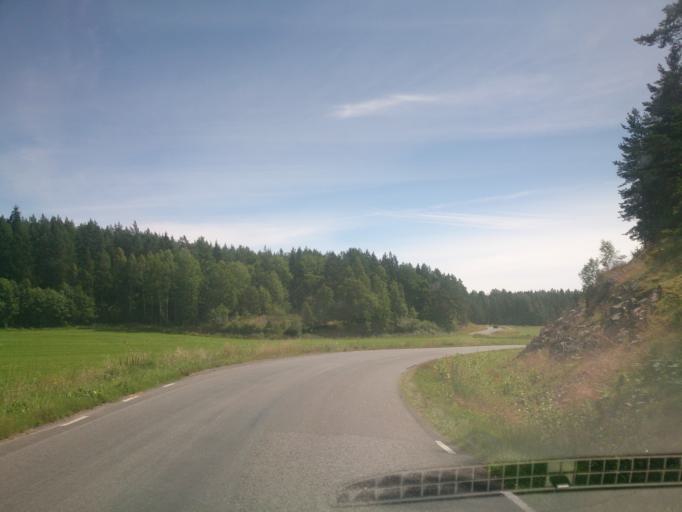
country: SE
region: OEstergoetland
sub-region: Valdemarsviks Kommun
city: Valdemarsvik
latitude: 58.2977
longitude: 16.6629
